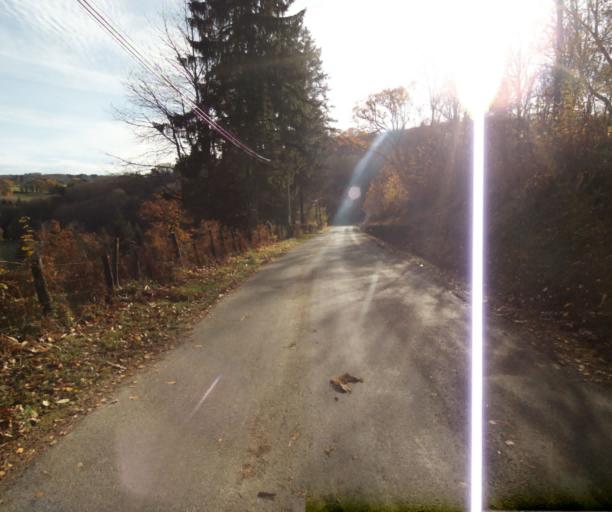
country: FR
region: Limousin
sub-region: Departement de la Correze
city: Sainte-Fortunade
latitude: 45.2097
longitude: 1.7537
